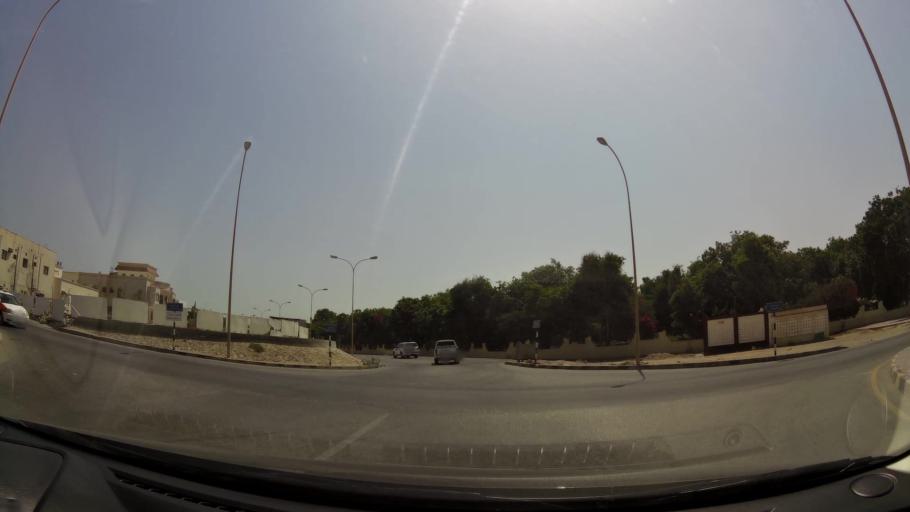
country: OM
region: Zufar
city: Salalah
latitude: 17.0119
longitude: 54.0731
